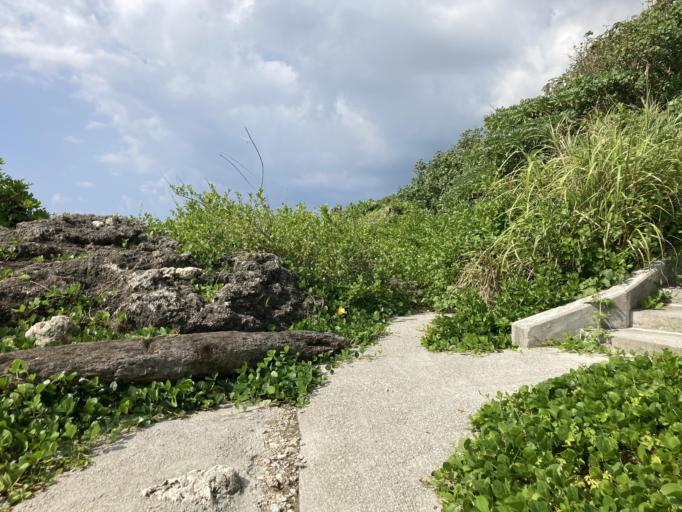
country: JP
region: Okinawa
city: Itoman
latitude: 26.1285
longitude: 127.7751
